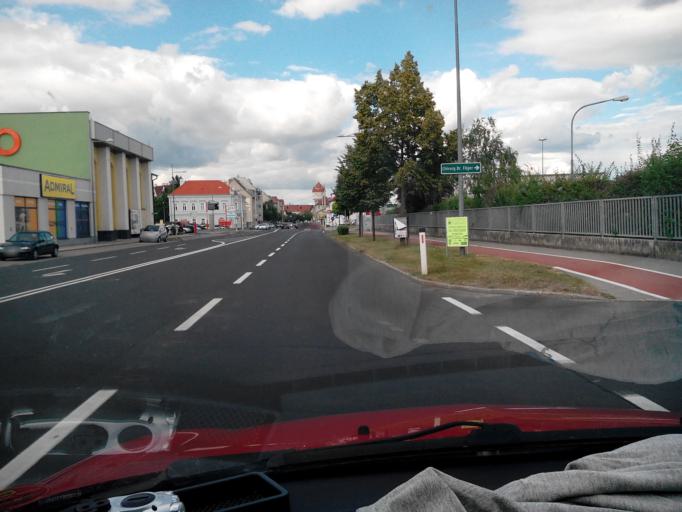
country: AT
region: Lower Austria
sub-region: Wiener Neustadt Stadt
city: Wiener Neustadt
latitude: 47.8035
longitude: 16.2349
